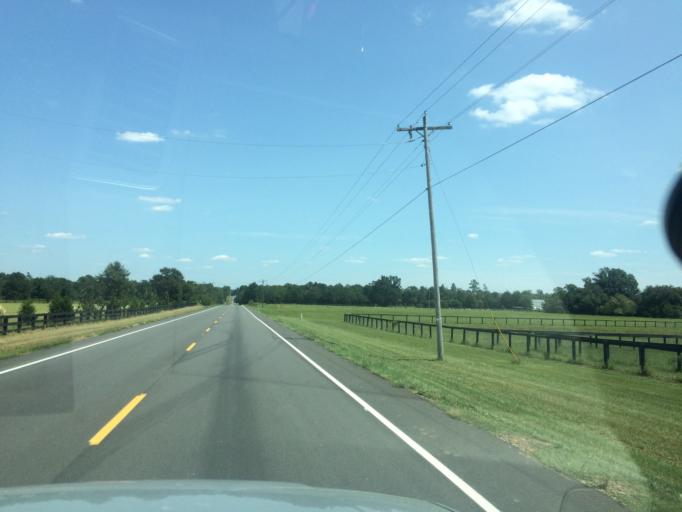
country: US
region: South Carolina
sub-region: Aiken County
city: Aiken
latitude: 33.5723
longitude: -81.5411
